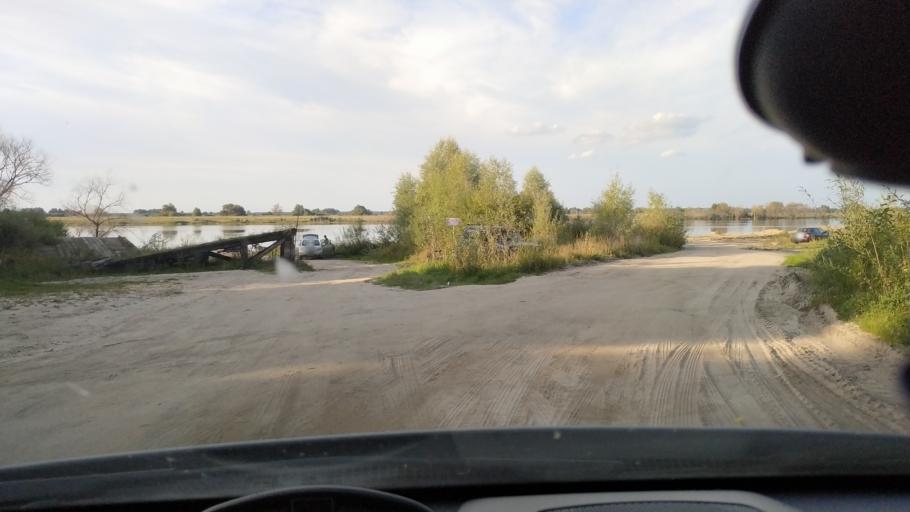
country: RU
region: Rjazan
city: Rybnoye
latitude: 54.8710
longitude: 39.6525
